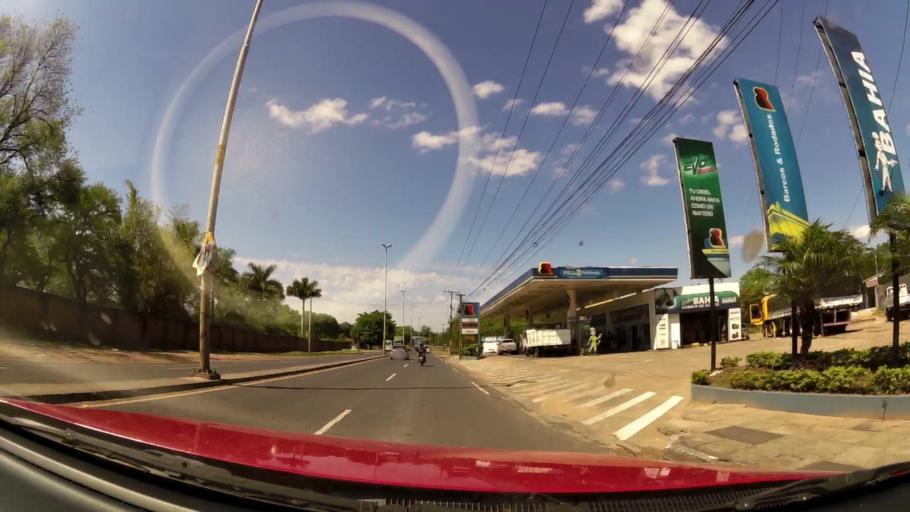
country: PY
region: Central
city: Colonia Mariano Roque Alonso
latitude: -25.2530
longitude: -57.5595
